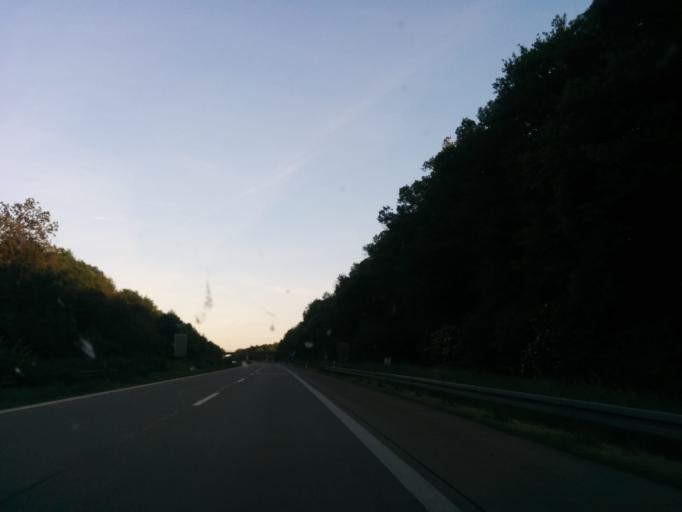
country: DE
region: Bavaria
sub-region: Regierungsbezirk Unterfranken
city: Sulzfeld am Main
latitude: 49.7104
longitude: 10.1035
